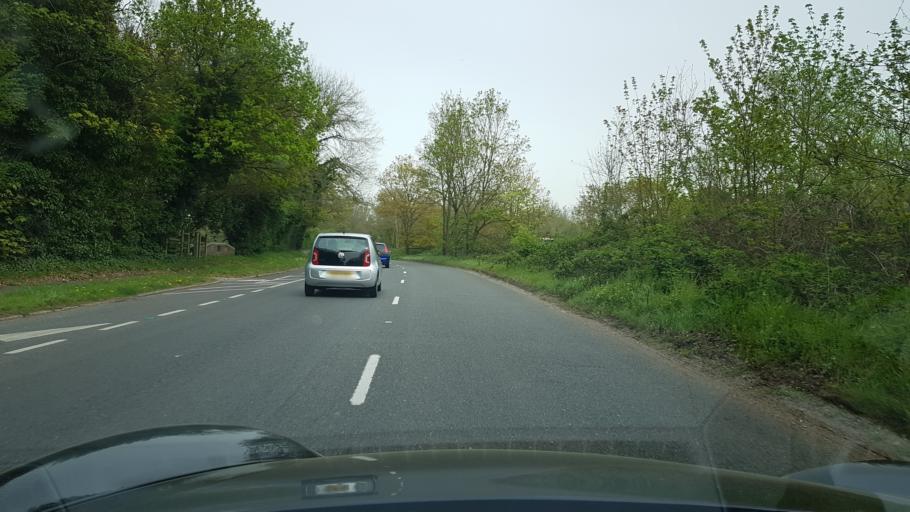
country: GB
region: England
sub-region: Surrey
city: Send
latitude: 51.2766
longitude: -0.5222
